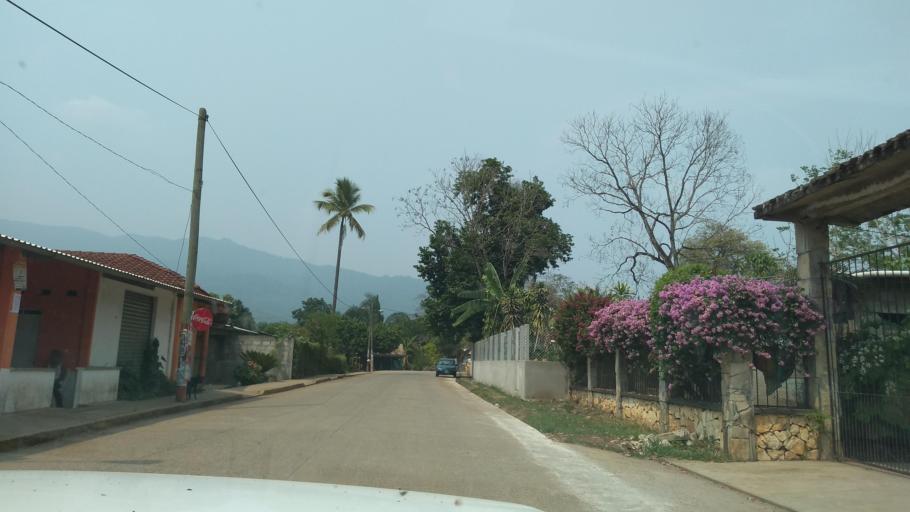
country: MX
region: Veracruz
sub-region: Tezonapa
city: Laguna Chica (Pueblo Nuevo)
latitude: 18.5438
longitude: -96.7788
